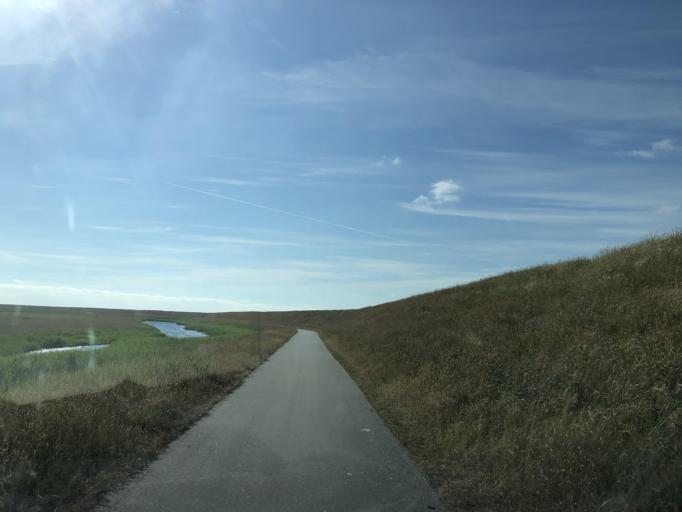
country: DK
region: South Denmark
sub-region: Esbjerg Kommune
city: Tjaereborg
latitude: 55.2935
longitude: 8.5639
